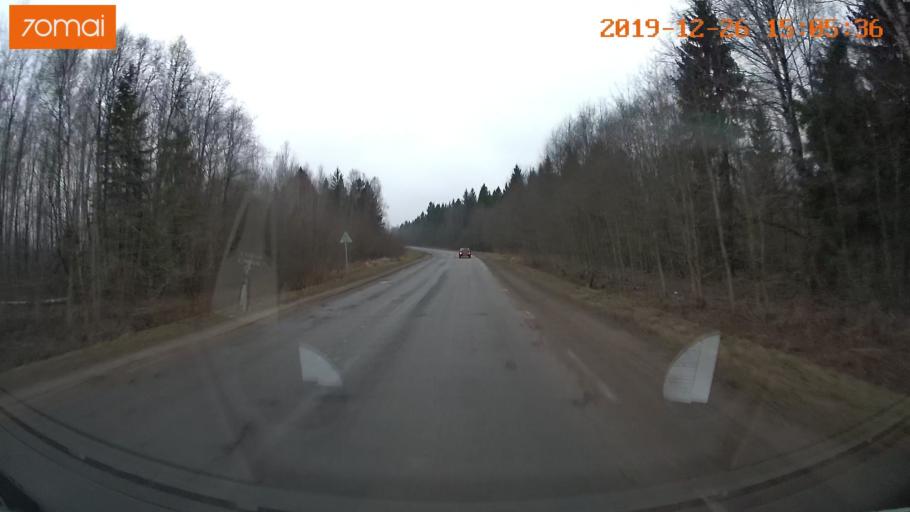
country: RU
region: Jaroslavl
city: Rybinsk
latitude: 58.1874
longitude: 38.8501
